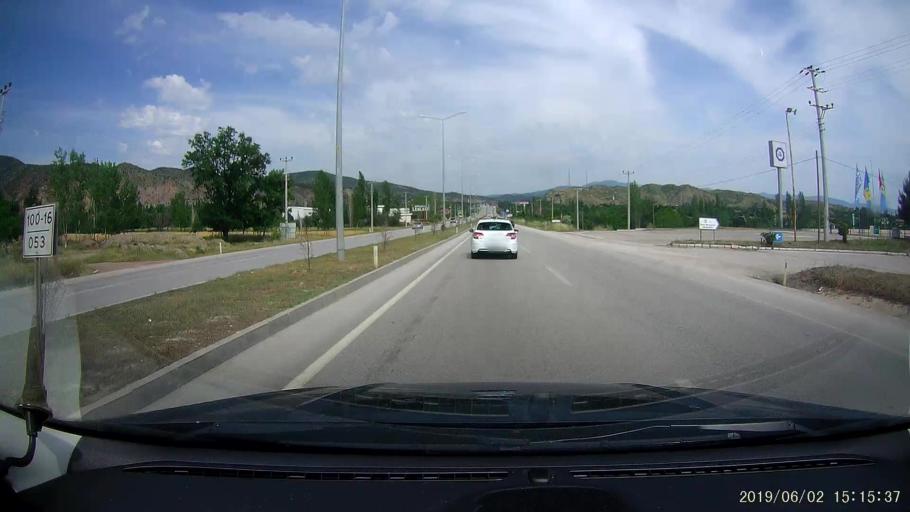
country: TR
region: Corum
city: Osmancik
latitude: 40.9703
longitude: 34.8523
